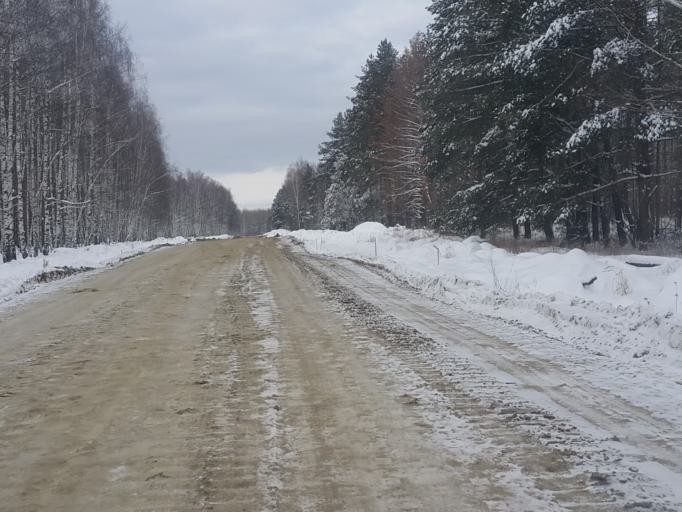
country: RU
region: Tambov
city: Platonovka
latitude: 52.8825
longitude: 41.8675
